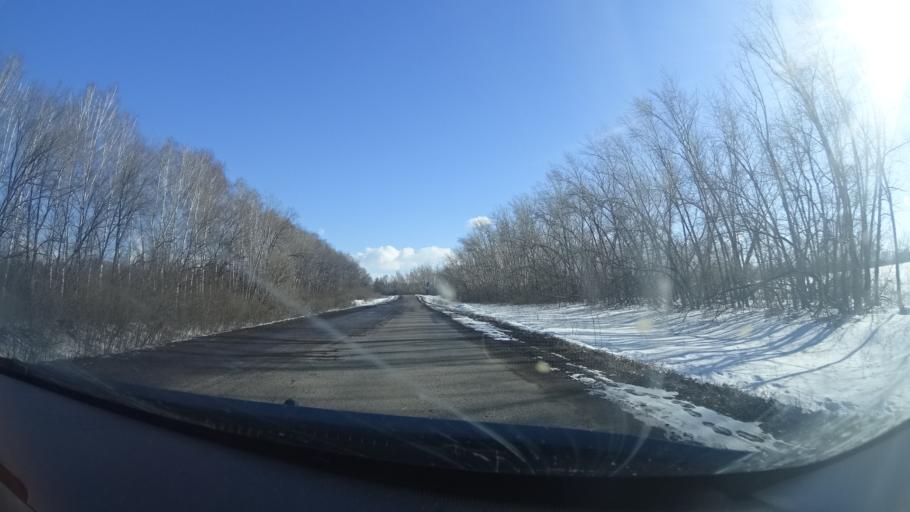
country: RU
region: Bashkortostan
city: Chishmy
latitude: 54.5995
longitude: 55.3510
